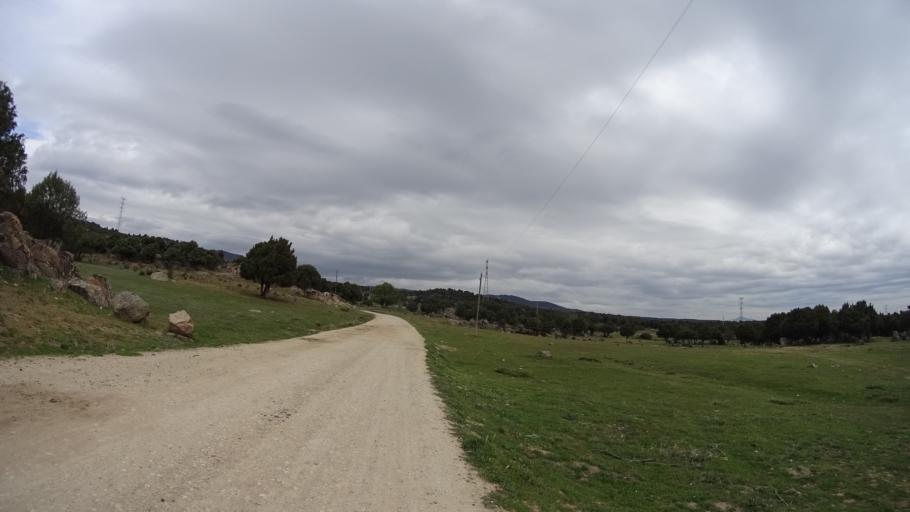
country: ES
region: Madrid
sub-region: Provincia de Madrid
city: Hoyo de Manzanares
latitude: 40.6092
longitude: -3.8771
